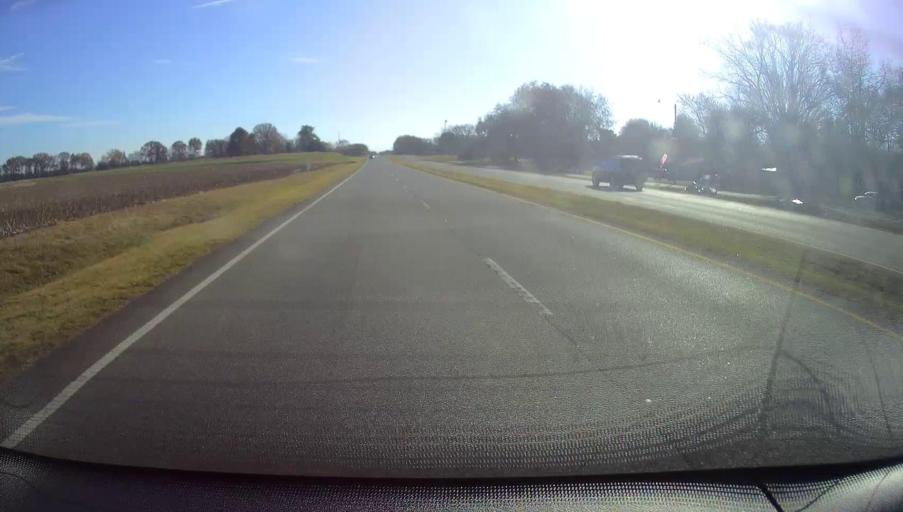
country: US
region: Alabama
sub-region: Morgan County
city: Decatur
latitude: 34.6383
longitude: -86.9506
